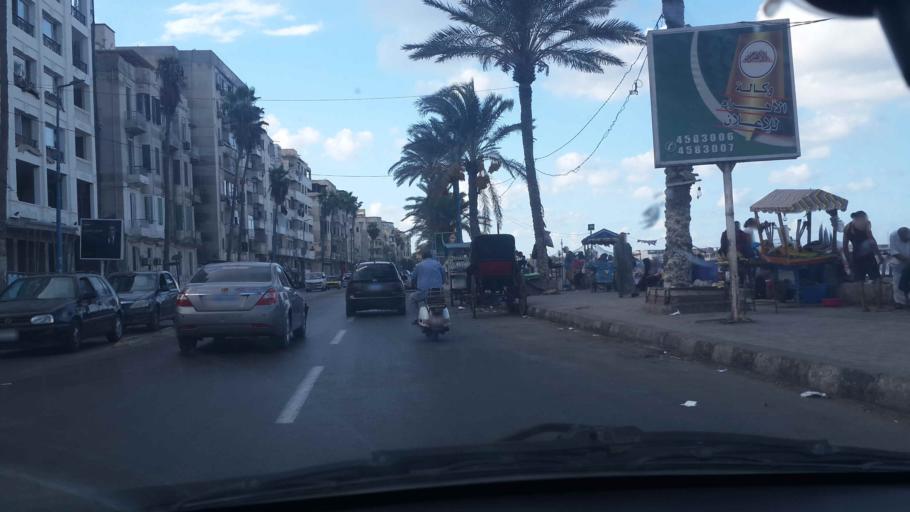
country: EG
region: Alexandria
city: Alexandria
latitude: 31.2068
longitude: 29.8839
